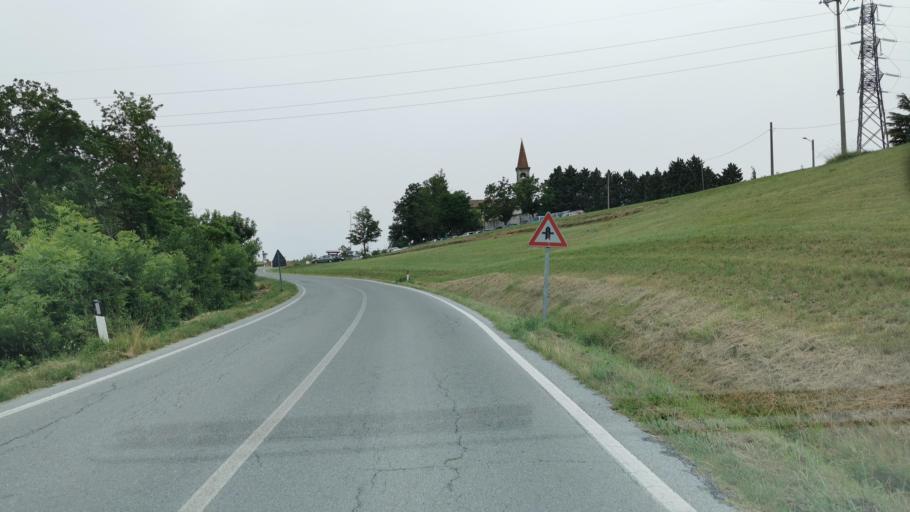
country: IT
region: Piedmont
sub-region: Provincia di Cuneo
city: Sale San Giovanni
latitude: 44.4026
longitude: 8.0764
